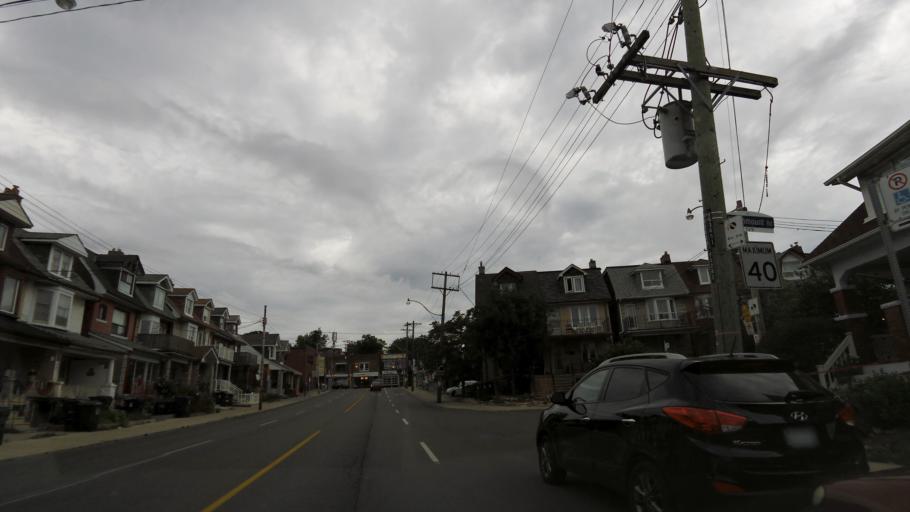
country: CA
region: Ontario
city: Toronto
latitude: 43.6738
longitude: -79.4306
